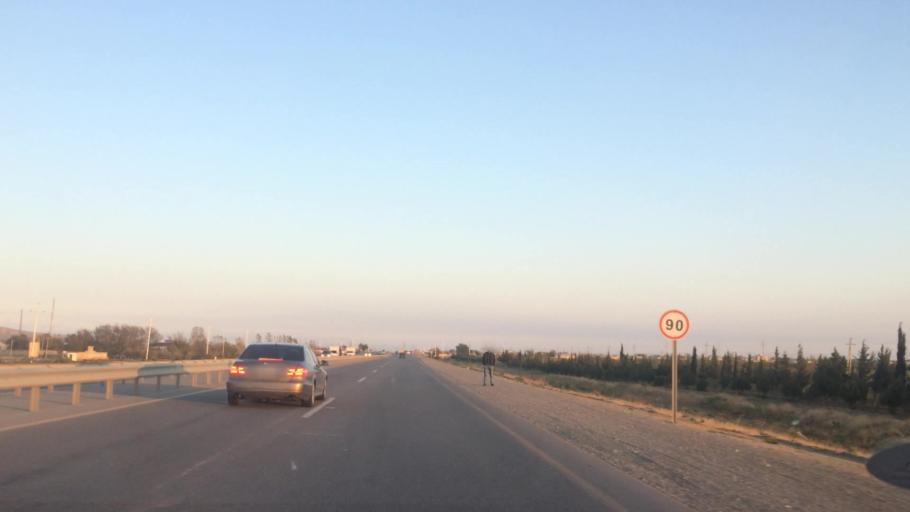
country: AZ
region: Baki
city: Qobustan
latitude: 39.9760
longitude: 49.2489
